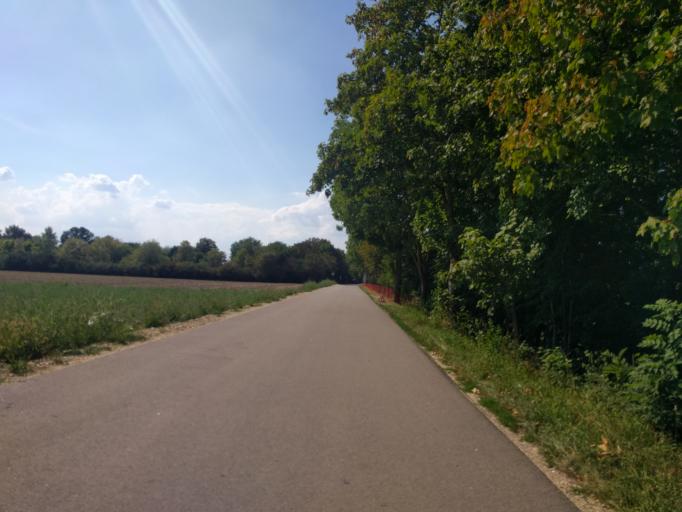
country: DE
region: Bavaria
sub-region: Upper Palatinate
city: Barbing
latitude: 49.0079
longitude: 12.2607
